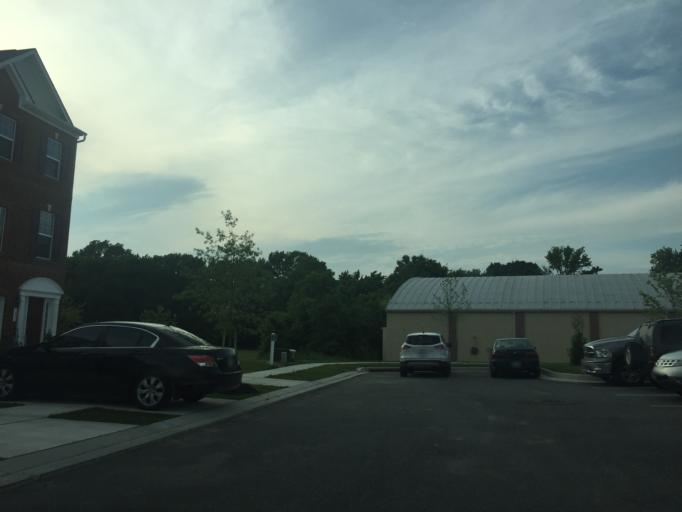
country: US
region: Maryland
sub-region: Baltimore County
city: Edgemere
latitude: 39.2703
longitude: -76.4734
